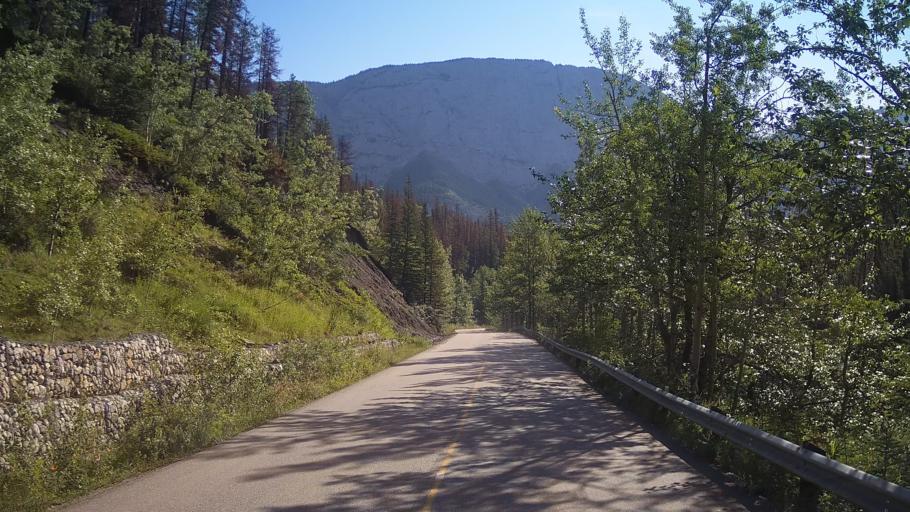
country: CA
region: Alberta
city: Hinton
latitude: 53.1770
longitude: -117.8522
